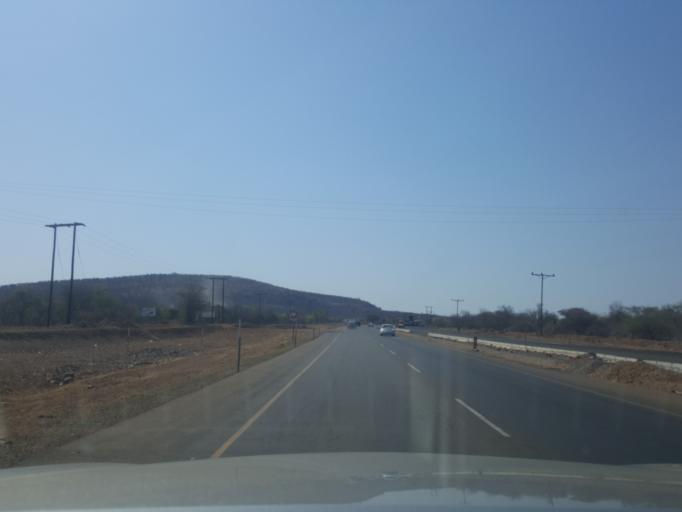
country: BW
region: Kweneng
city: Gabane
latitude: -24.7591
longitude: 25.8302
